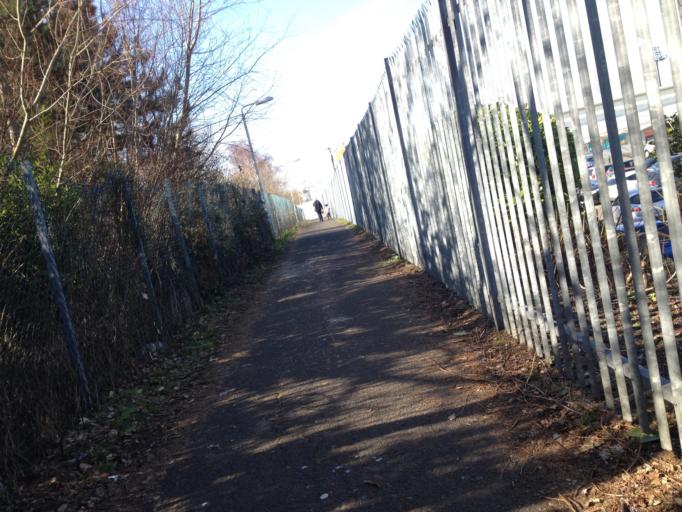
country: GB
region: Scotland
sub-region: South Lanarkshire
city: Hamilton
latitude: 55.7798
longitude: -4.0558
